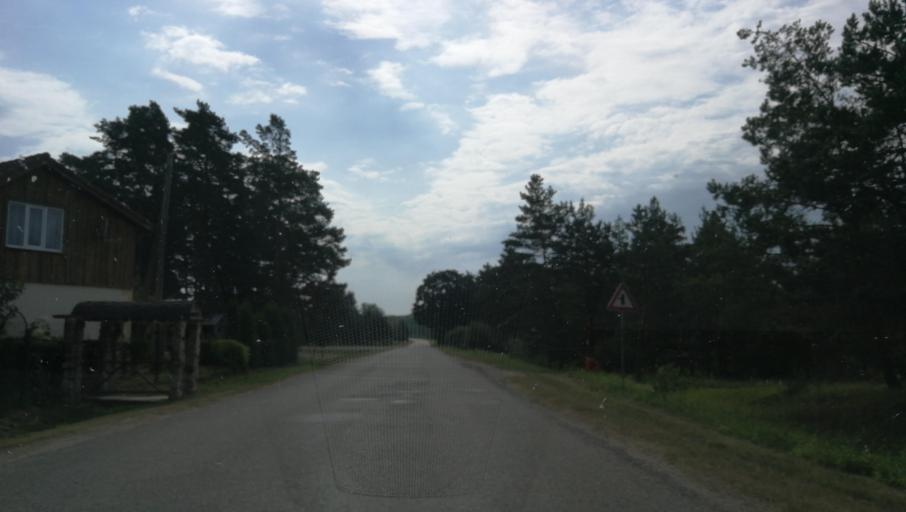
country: LV
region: Alsunga
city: Alsunga
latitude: 56.9779
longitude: 21.5547
